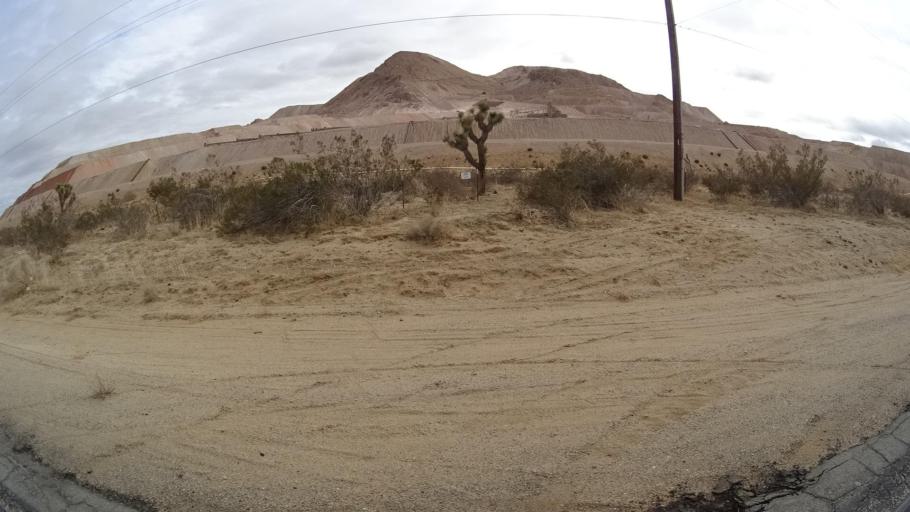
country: US
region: California
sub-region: Kern County
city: Mojave
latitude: 34.9956
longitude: -118.1994
